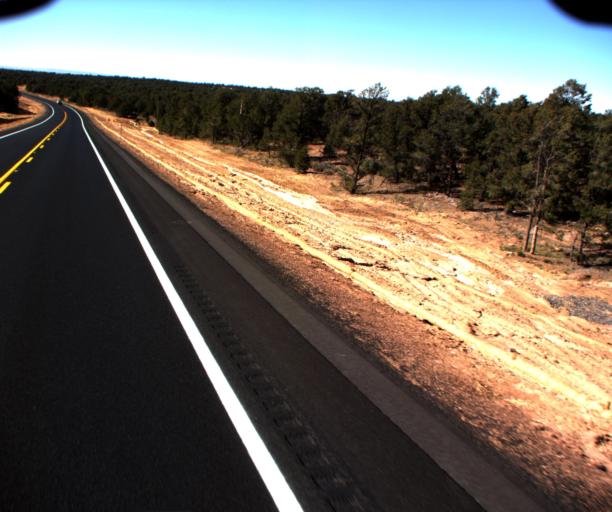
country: US
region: Arizona
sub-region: Apache County
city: Ganado
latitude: 35.7145
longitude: -109.3373
